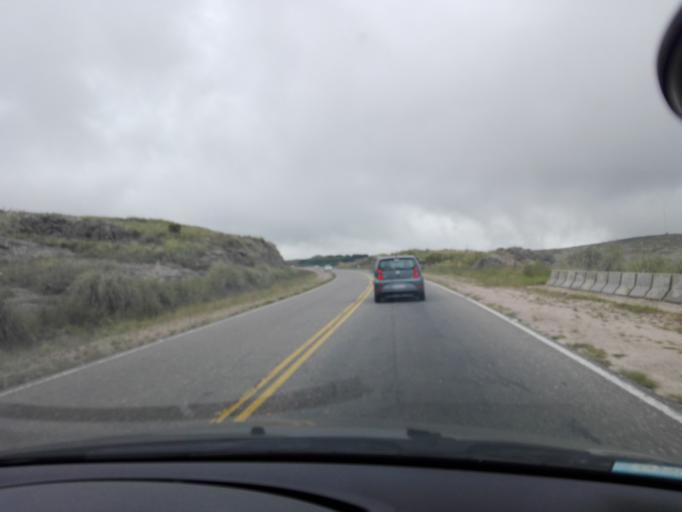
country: AR
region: Cordoba
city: Cuesta Blanca
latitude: -31.6103
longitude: -64.7498
